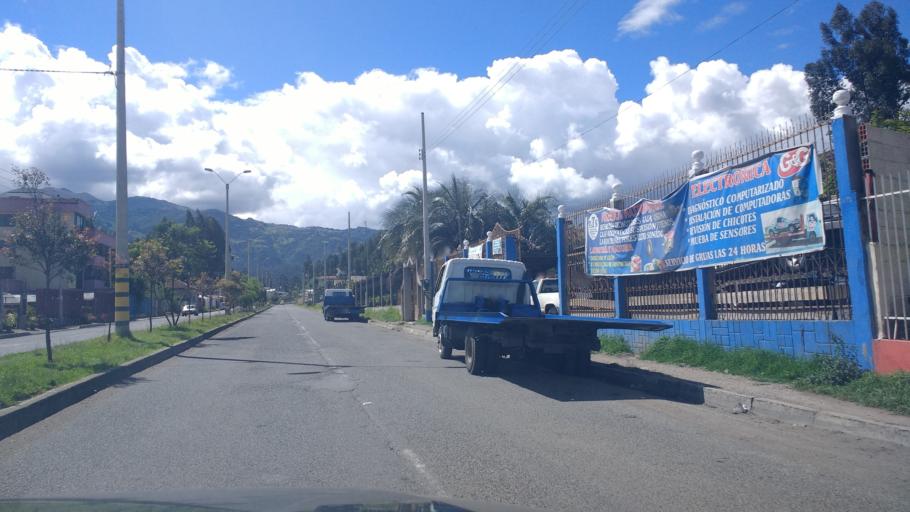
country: EC
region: Azuay
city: Cuenca
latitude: -2.9023
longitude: -79.0405
